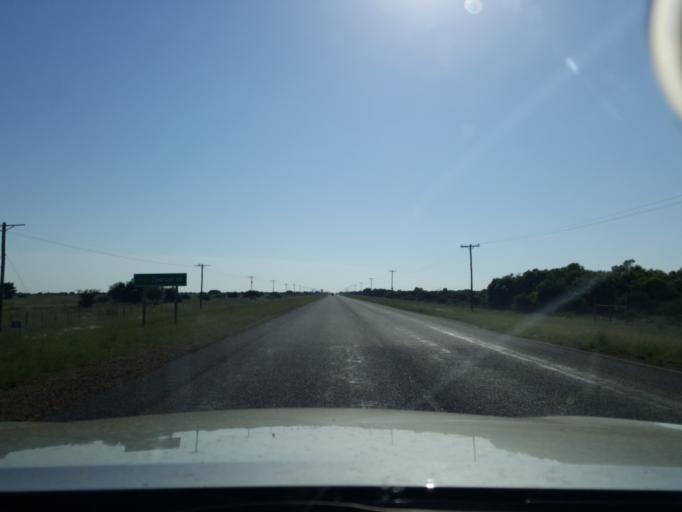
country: ZA
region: North-West
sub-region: Ngaka Modiri Molema District Municipality
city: Mahikeng
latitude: -25.8448
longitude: 25.7119
